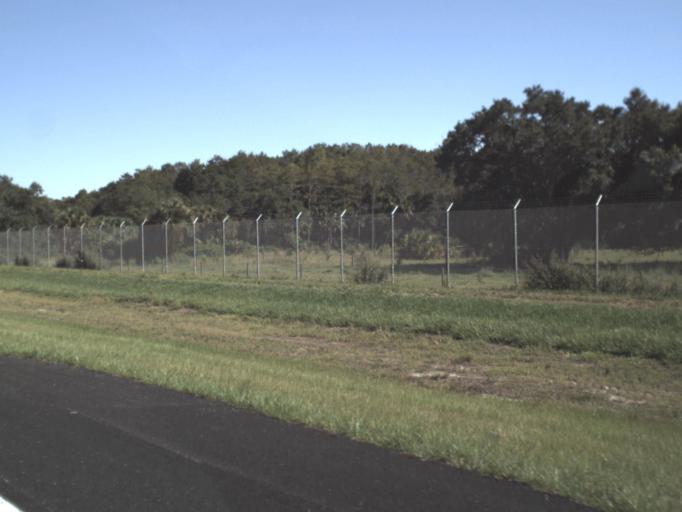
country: US
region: Florida
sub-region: Hendry County
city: Port LaBelle
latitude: 26.7683
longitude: -81.3367
